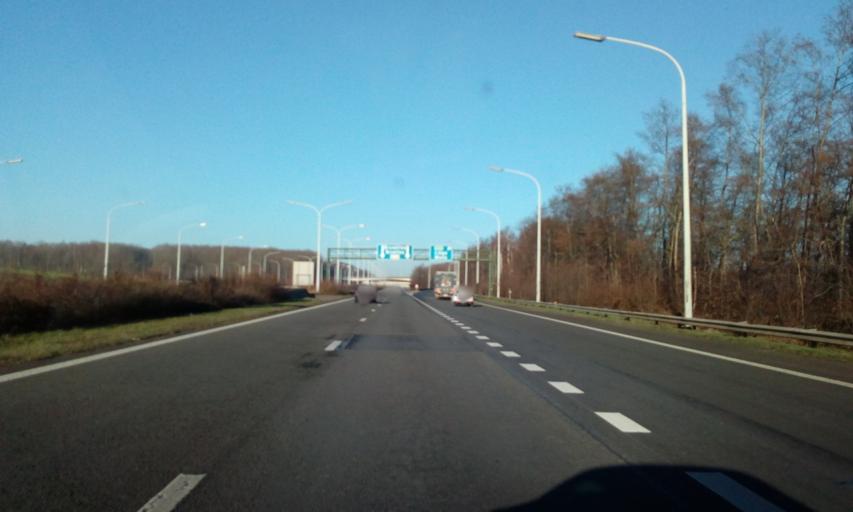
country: BE
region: Wallonia
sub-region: Province du Hainaut
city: Brunehault
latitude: 50.4685
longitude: 4.4168
